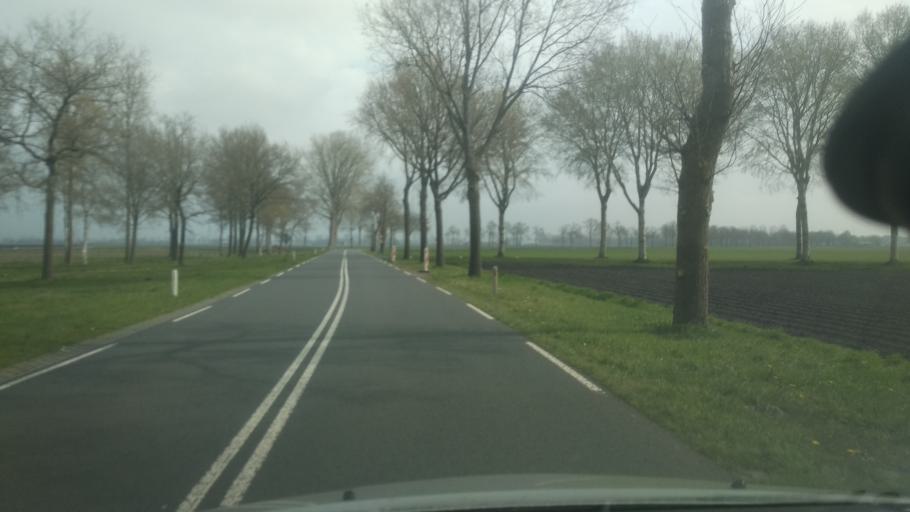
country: NL
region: Drenthe
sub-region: Gemeente Borger-Odoorn
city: Borger
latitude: 52.8952
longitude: 6.8938
